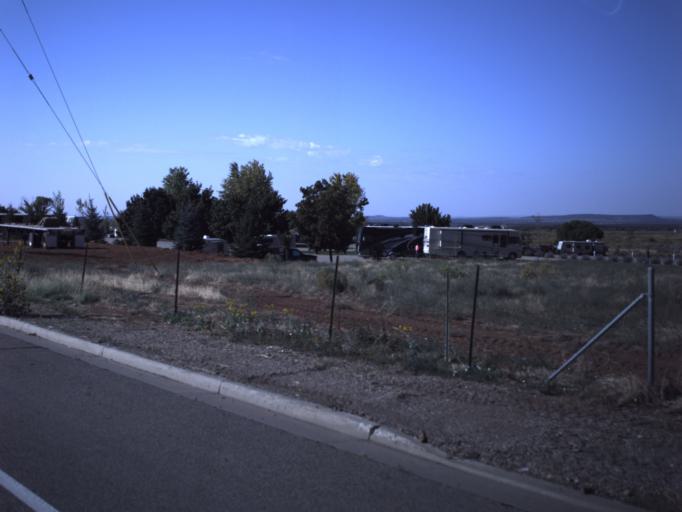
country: US
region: Utah
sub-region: San Juan County
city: Blanding
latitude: 37.5990
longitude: -109.4787
